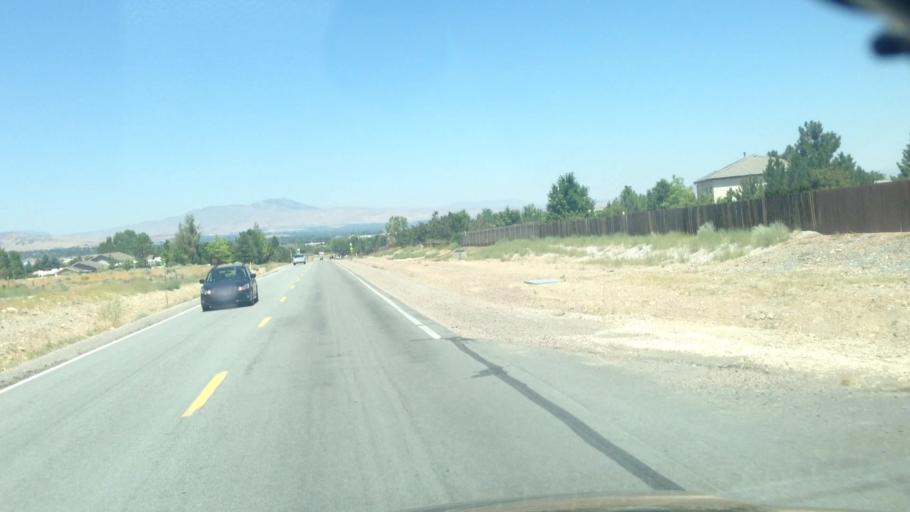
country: US
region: Nevada
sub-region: Storey County
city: Virginia City
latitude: 39.3903
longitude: -119.7298
